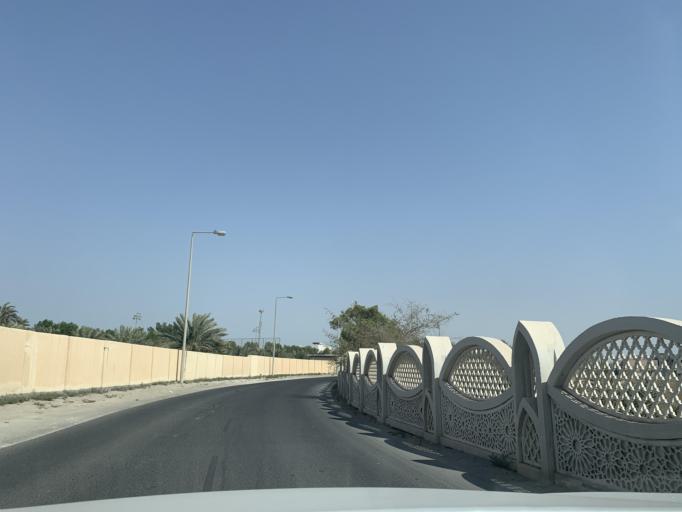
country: BH
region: Manama
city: Jidd Hafs
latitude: 26.2262
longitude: 50.4648
